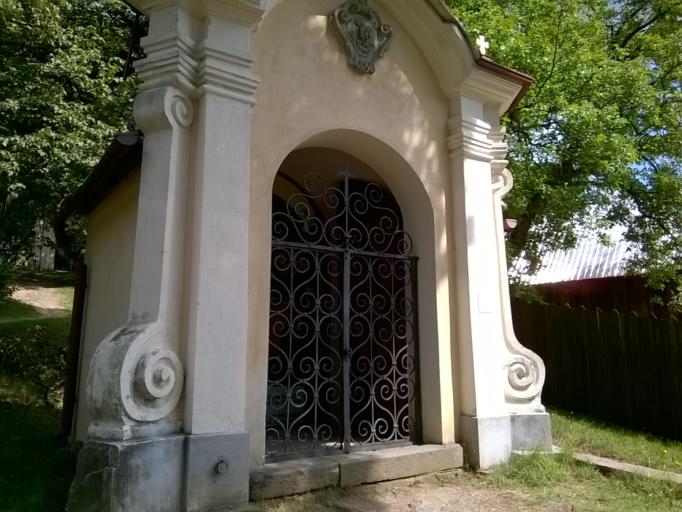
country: SK
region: Banskobystricky
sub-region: Okres Banska Bystrica
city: Banska Stiavnica
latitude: 48.4617
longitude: 18.9094
